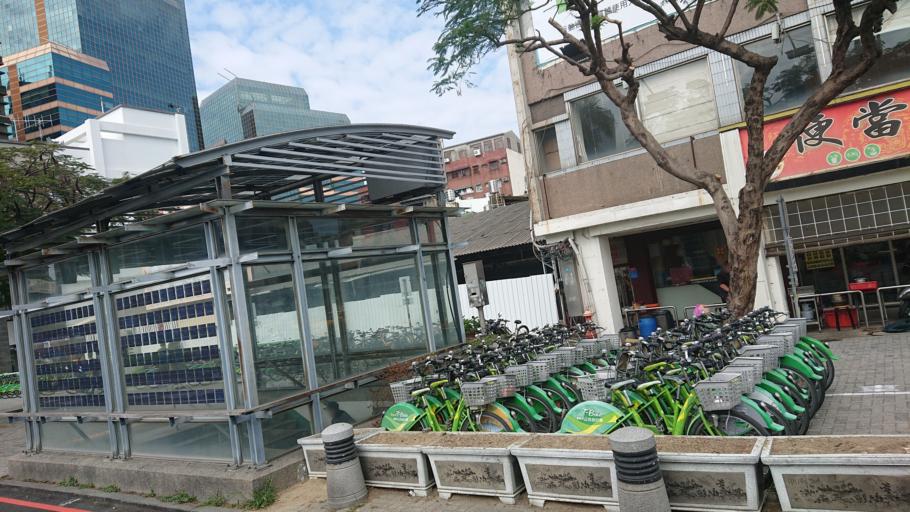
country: TW
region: Taiwan
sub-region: Tainan
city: Tainan
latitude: 22.9977
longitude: 120.2121
